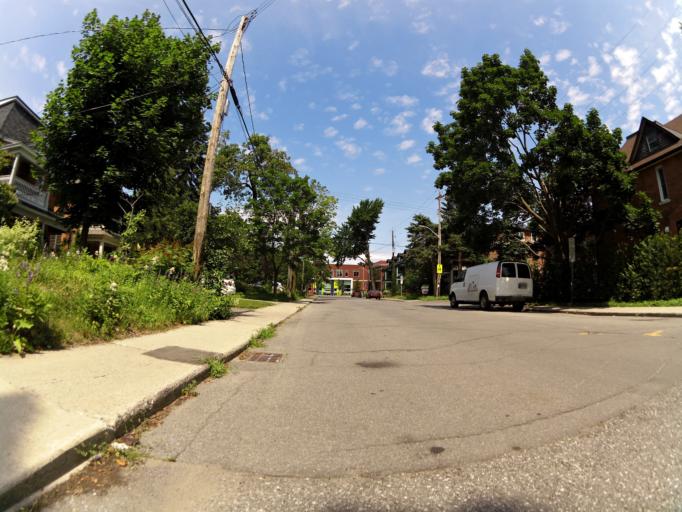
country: CA
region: Ontario
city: Ottawa
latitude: 45.3996
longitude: -75.6902
